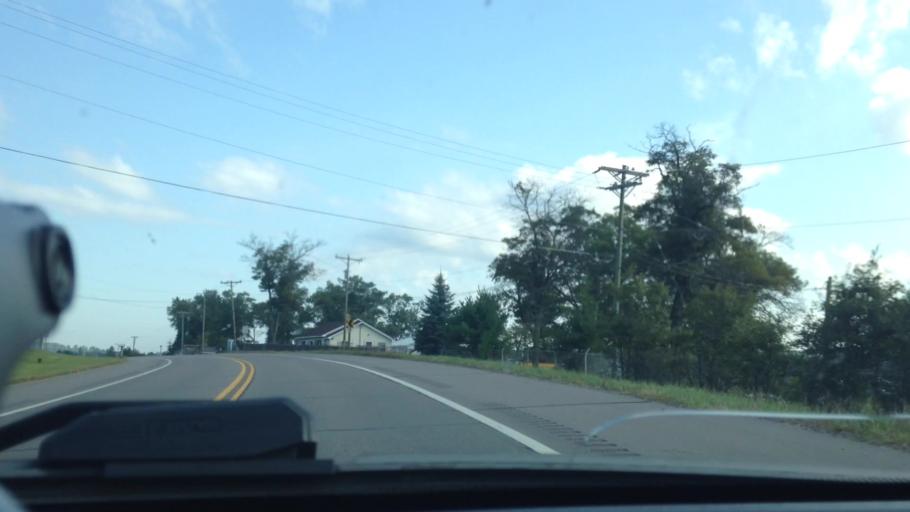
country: US
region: Michigan
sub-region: Dickinson County
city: Norway
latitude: 45.7707
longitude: -87.9092
